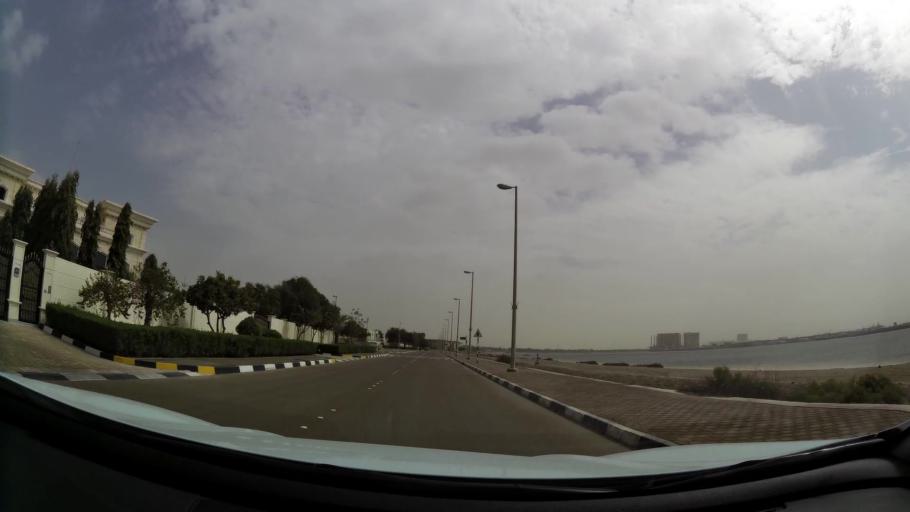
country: AE
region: Abu Dhabi
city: Abu Dhabi
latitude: 24.3924
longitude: 54.5064
